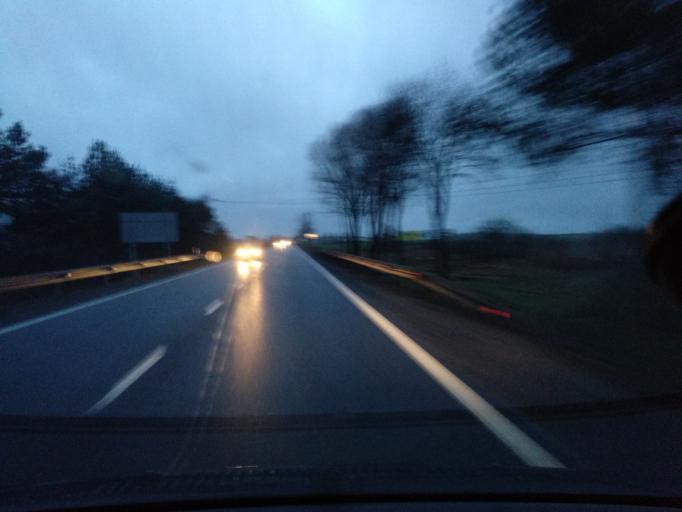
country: PL
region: Lower Silesian Voivodeship
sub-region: Powiat sredzki
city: Malczyce
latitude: 51.1954
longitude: 16.4989
